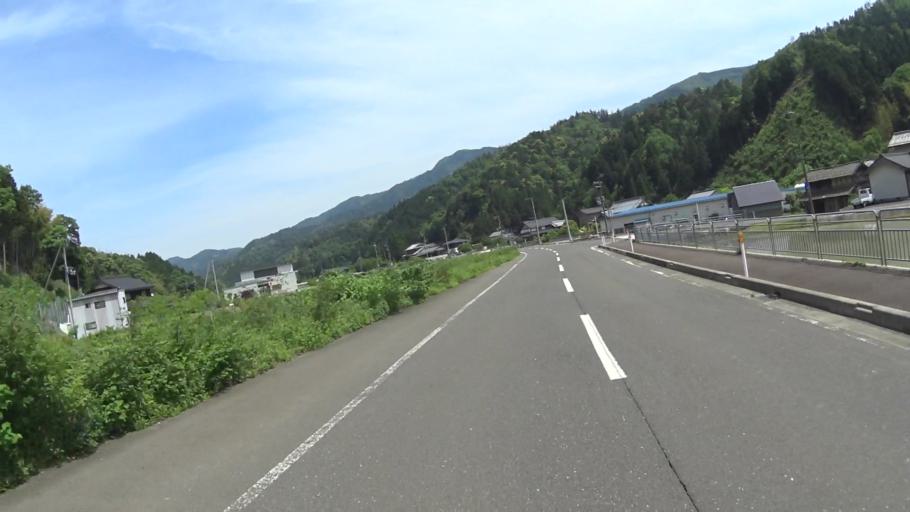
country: JP
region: Kyoto
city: Maizuru
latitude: 35.4407
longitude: 135.5244
